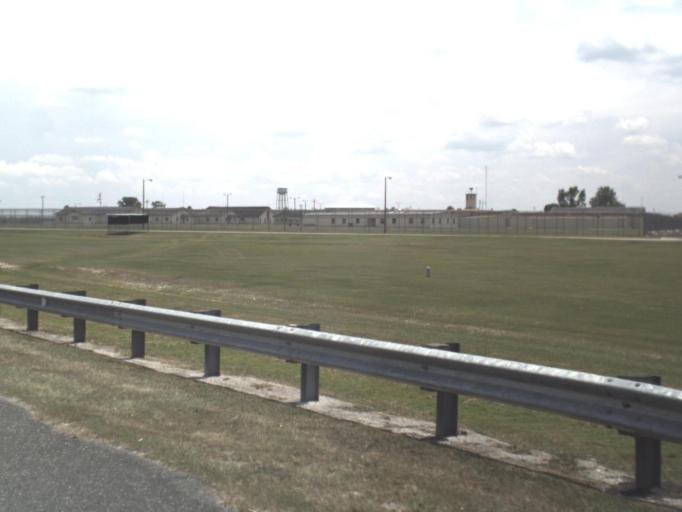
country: US
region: Florida
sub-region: Bradford County
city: Starke
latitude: 30.0656
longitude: -82.1832
